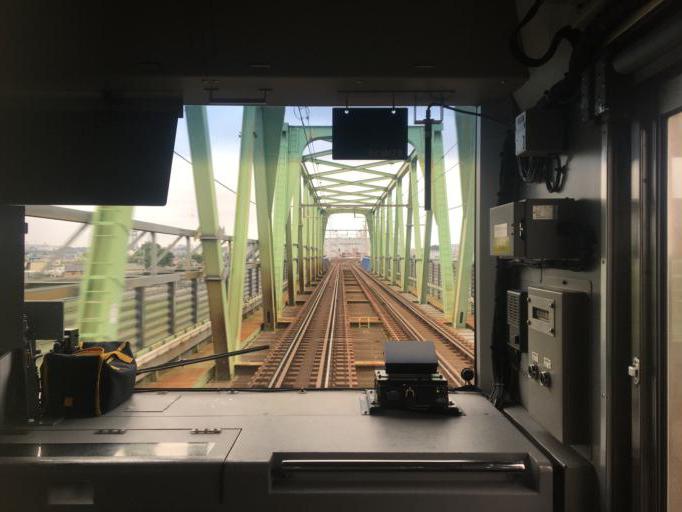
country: JP
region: Saitama
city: Asaka
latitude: 35.8301
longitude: 139.6124
